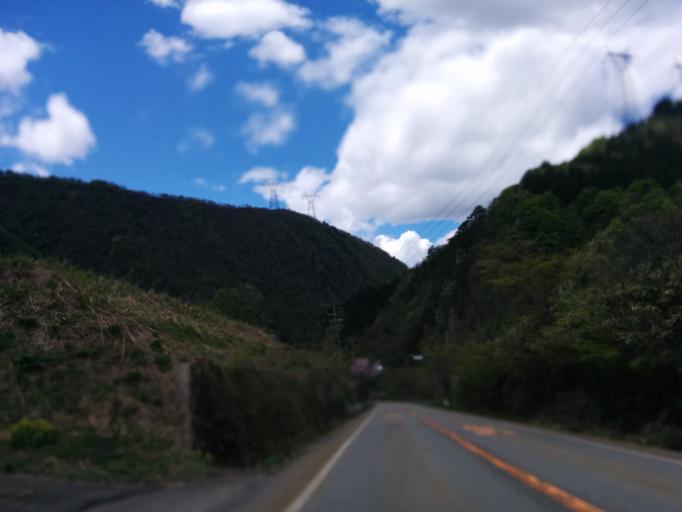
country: JP
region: Toyama
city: Fukumitsu
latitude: 36.3201
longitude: 136.8988
